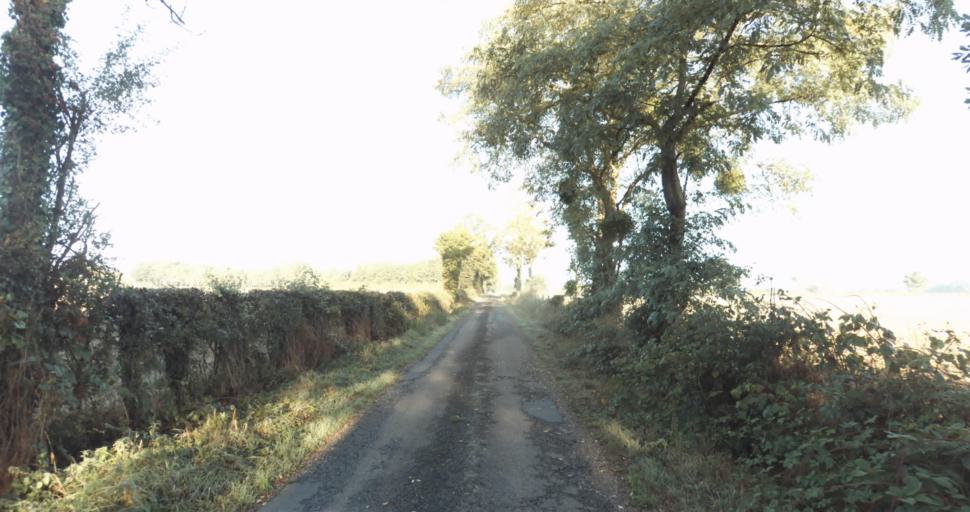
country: FR
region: Lower Normandy
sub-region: Departement de l'Orne
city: Vimoutiers
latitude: 48.9146
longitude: 0.1563
